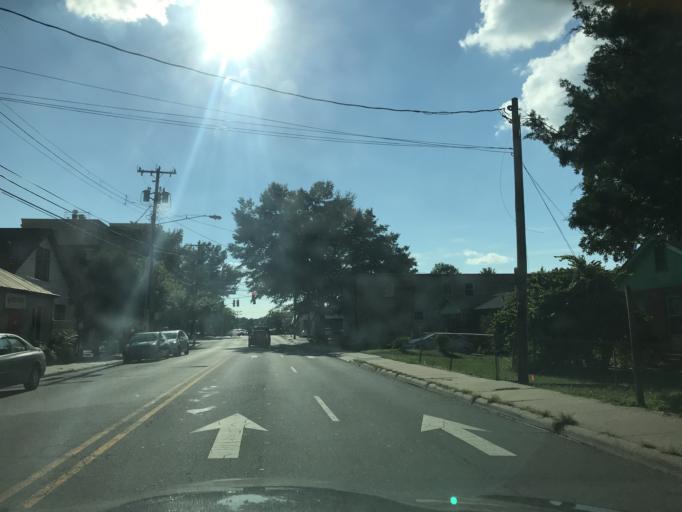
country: US
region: North Carolina
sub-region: Orange County
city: Carrboro
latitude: 35.9110
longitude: -79.0662
